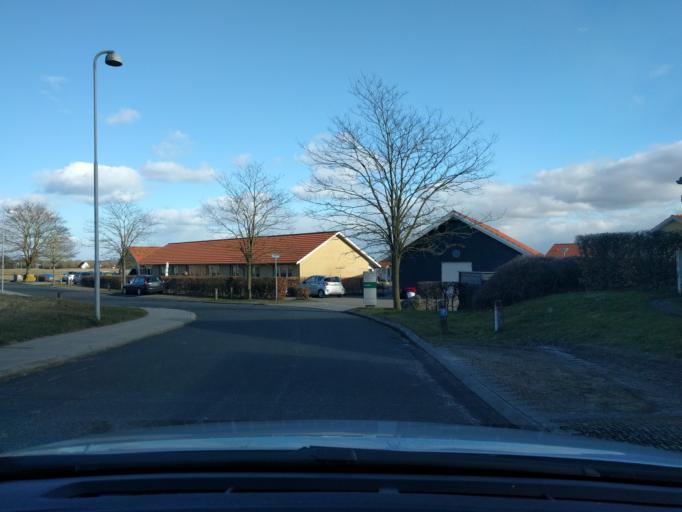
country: DK
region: South Denmark
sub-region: Kerteminde Kommune
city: Munkebo
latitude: 55.4591
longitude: 10.5642
